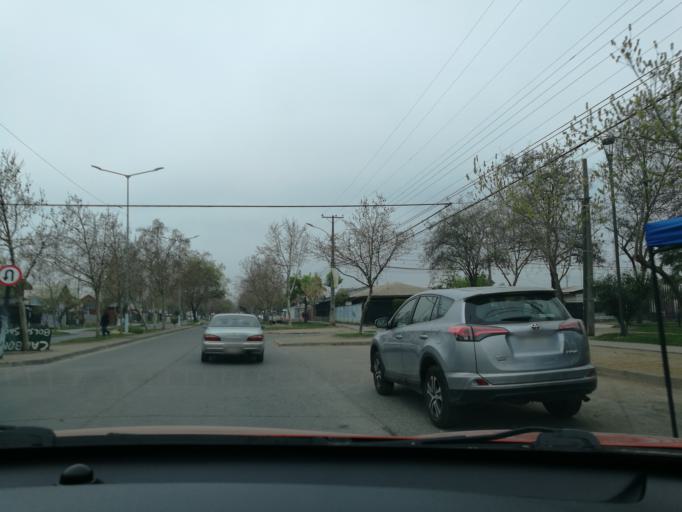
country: CL
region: O'Higgins
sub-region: Provincia de Cachapoal
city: Rancagua
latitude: -34.1635
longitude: -70.7226
